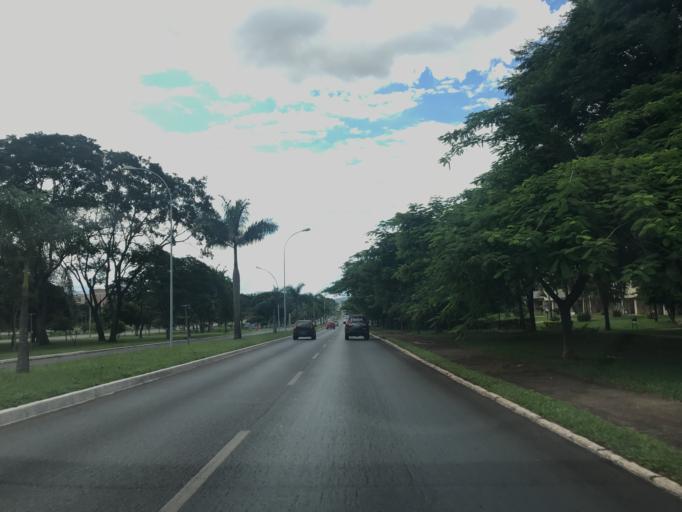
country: BR
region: Federal District
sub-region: Brasilia
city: Brasilia
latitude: -15.7546
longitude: -47.8858
